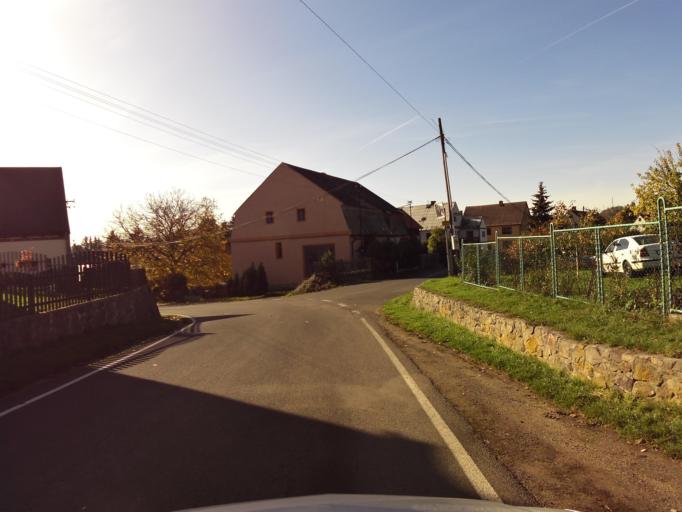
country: CZ
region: Ustecky
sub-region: Okres Chomutov
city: Perstejn
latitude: 50.3887
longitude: 13.1335
